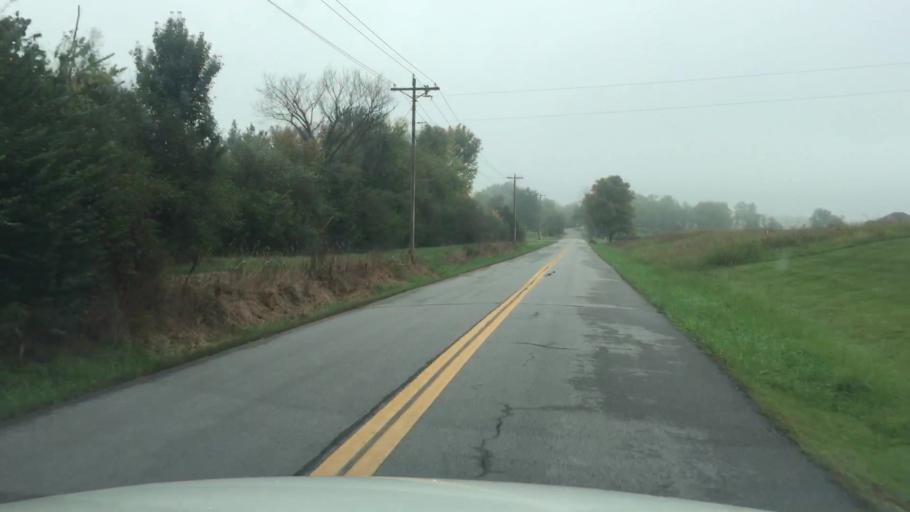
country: US
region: Missouri
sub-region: Boone County
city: Ashland
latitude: 38.8515
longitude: -92.3060
